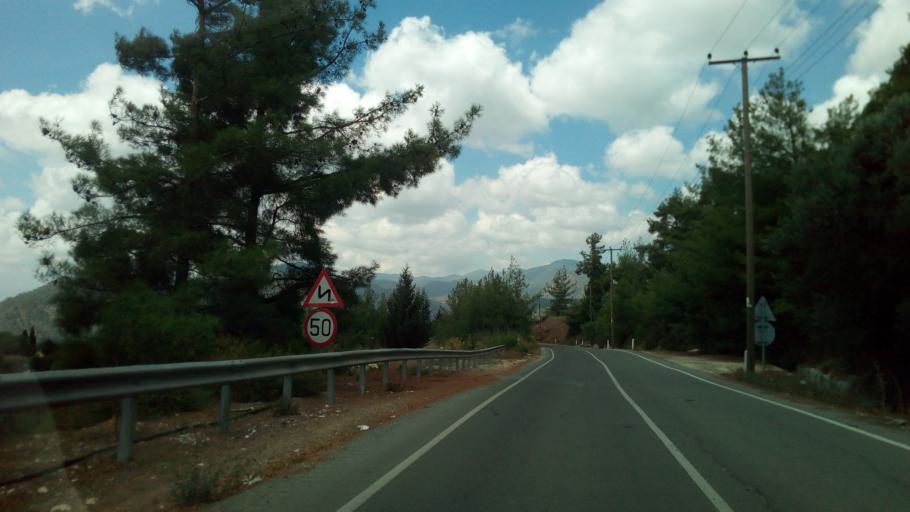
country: CY
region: Pafos
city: Mesogi
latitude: 34.9218
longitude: 32.6249
